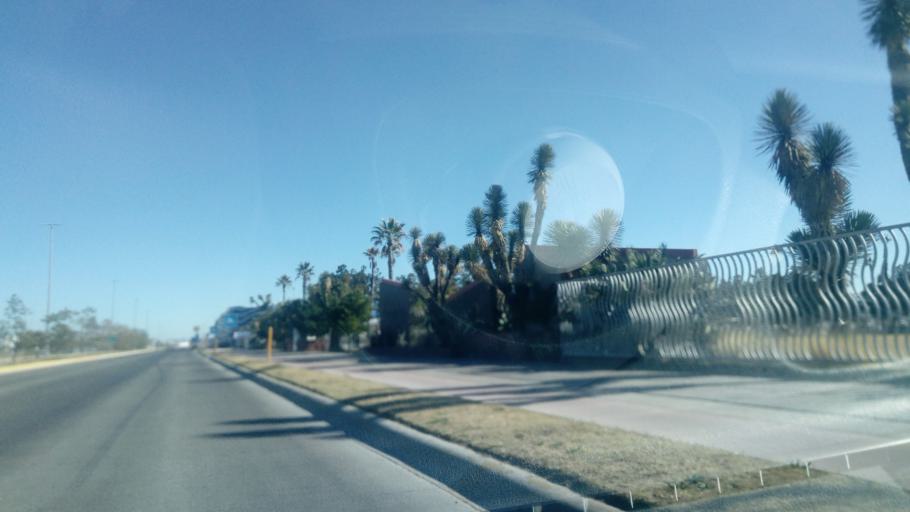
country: MX
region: Durango
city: Victoria de Durango
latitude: 24.0823
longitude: -104.5862
